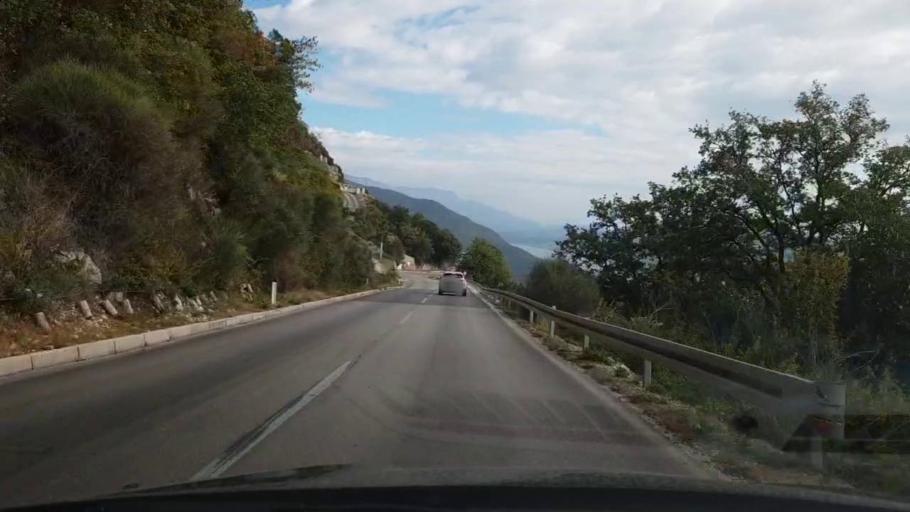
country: ME
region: Herceg Novi
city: Herceg-Novi
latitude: 42.4689
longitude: 18.5409
